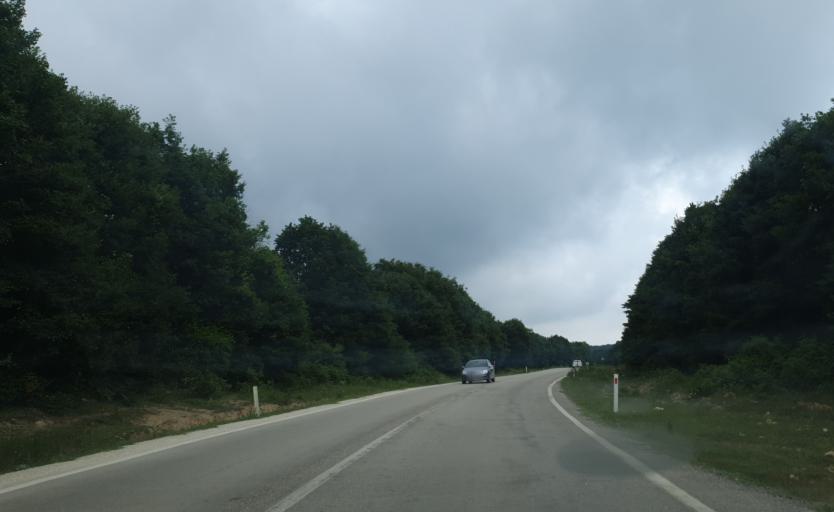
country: TR
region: Kirklareli
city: Salmydessus
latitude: 41.5658
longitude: 28.0712
